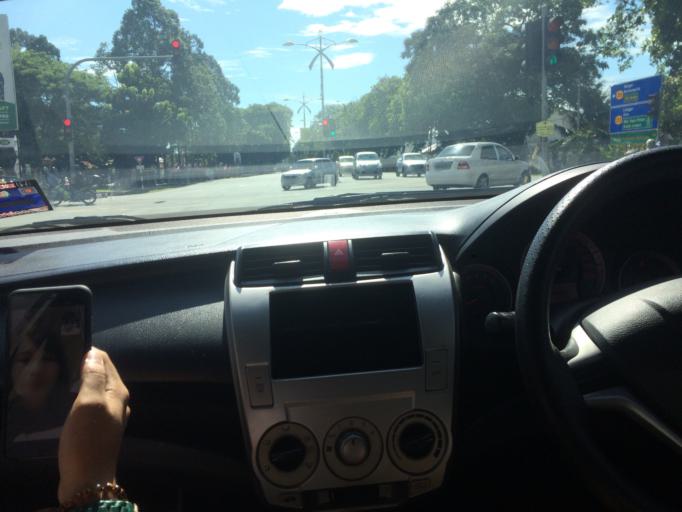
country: MY
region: Kedah
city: Alor Setar
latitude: 6.1442
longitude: 100.3768
